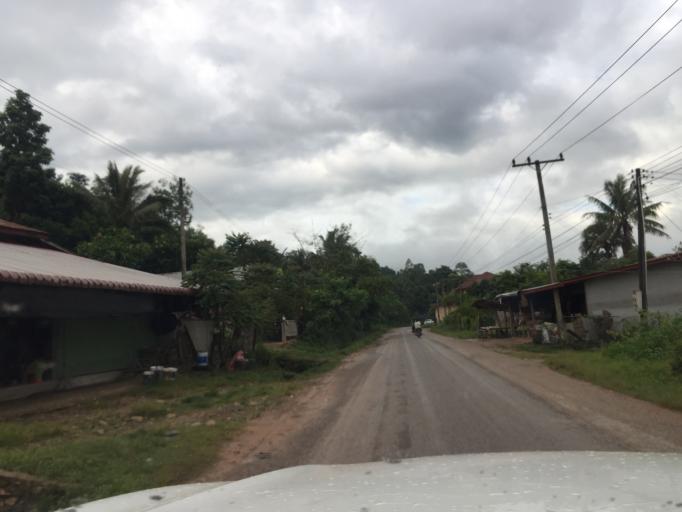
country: LA
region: Oudomxai
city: Muang La
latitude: 20.8619
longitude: 102.1156
